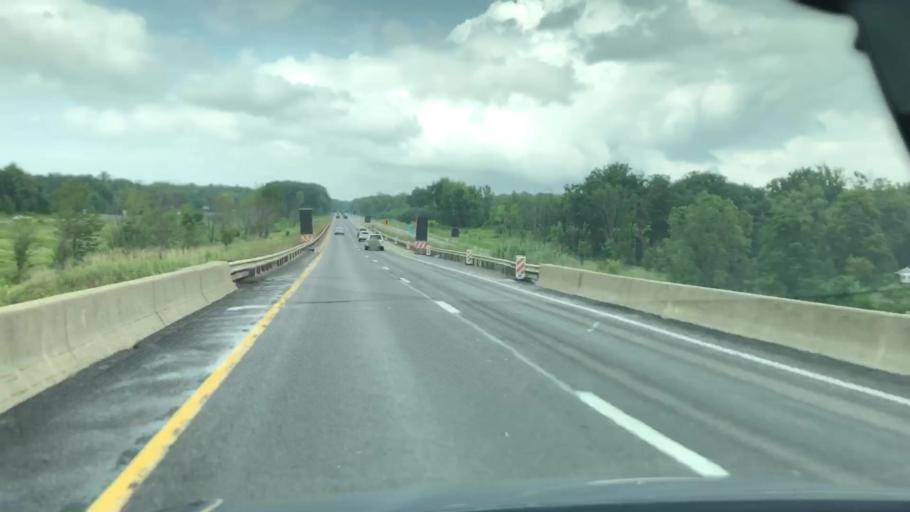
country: US
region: Pennsylvania
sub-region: Erie County
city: Fairview
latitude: 41.9974
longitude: -80.1650
